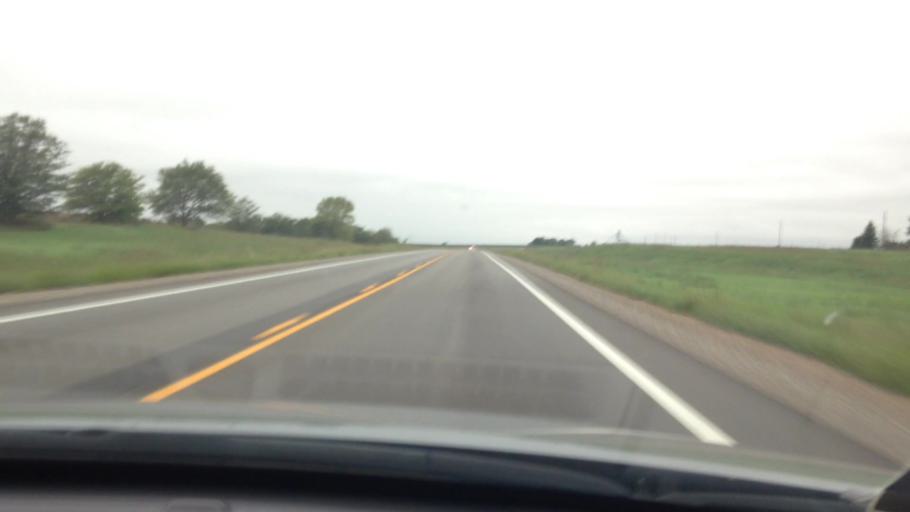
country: US
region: Kansas
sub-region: Doniphan County
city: Highland
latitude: 39.8412
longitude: -95.3886
